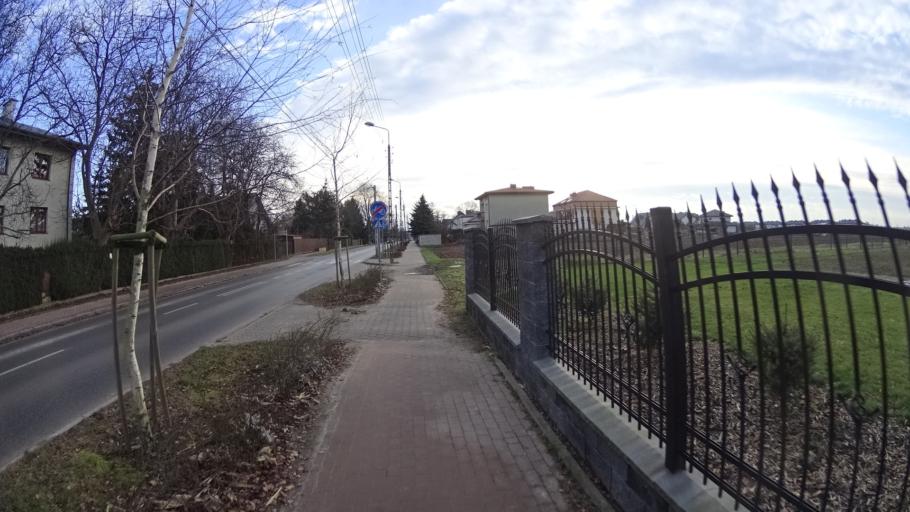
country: PL
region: Masovian Voivodeship
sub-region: Powiat warszawski zachodni
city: Ozarow Mazowiecki
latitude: 52.2237
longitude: 20.8013
